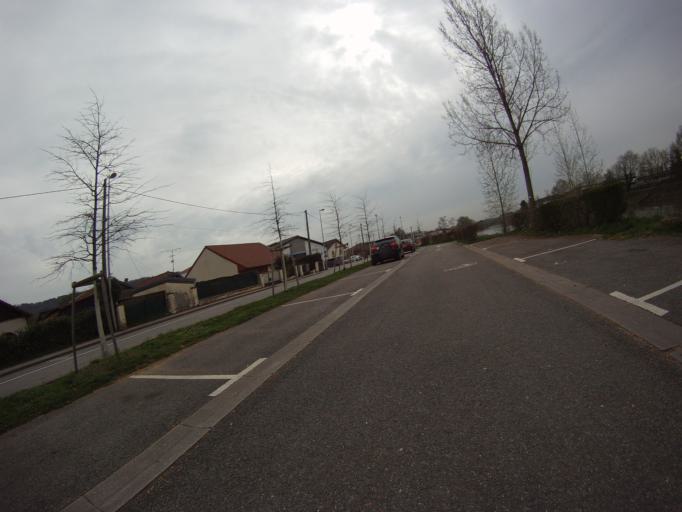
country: FR
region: Lorraine
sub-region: Departement de Meurthe-et-Moselle
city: Malzeville
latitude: 48.7131
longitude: 6.1763
